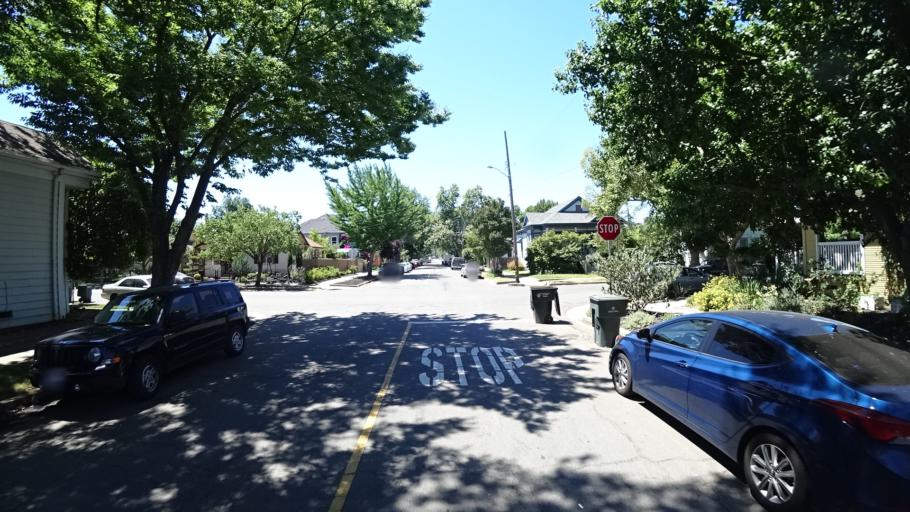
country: US
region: California
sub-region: Sacramento County
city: Sacramento
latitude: 38.5565
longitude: -121.4693
